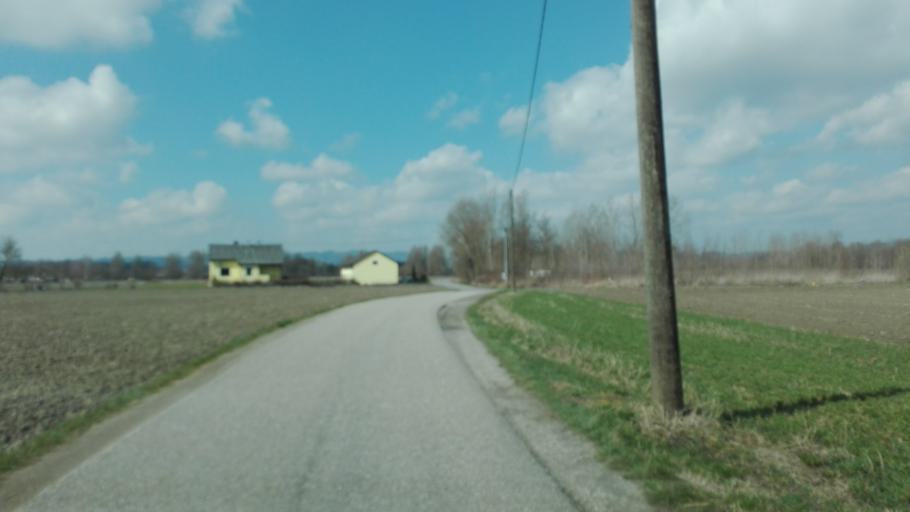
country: AT
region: Upper Austria
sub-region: Politischer Bezirk Urfahr-Umgebung
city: Goldworth
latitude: 48.3302
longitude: 14.0807
